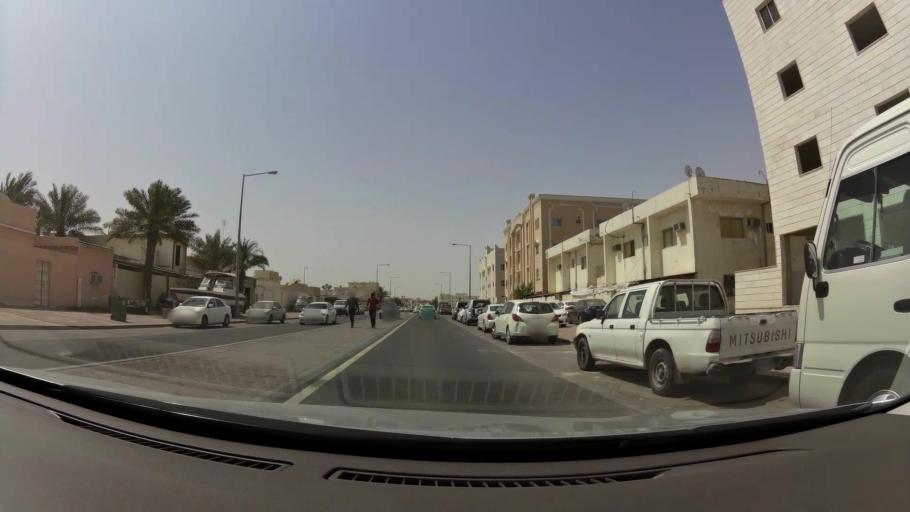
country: QA
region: Baladiyat ad Dawhah
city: Doha
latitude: 25.3208
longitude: 51.4820
